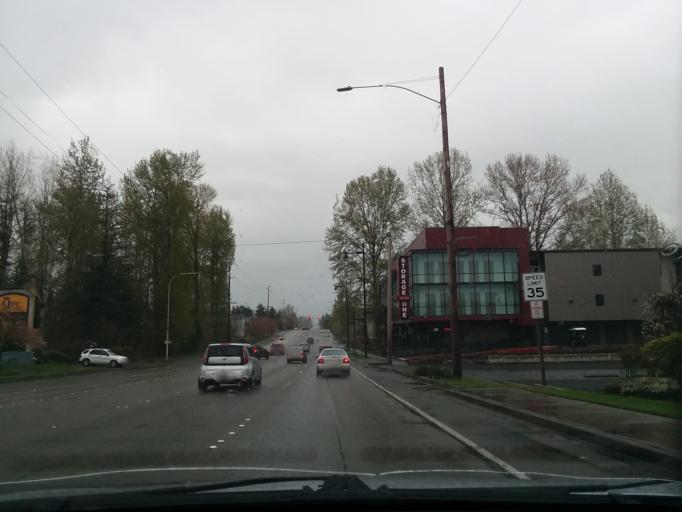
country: US
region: Washington
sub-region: King County
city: Fairwood
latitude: 47.4884
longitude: -122.1552
